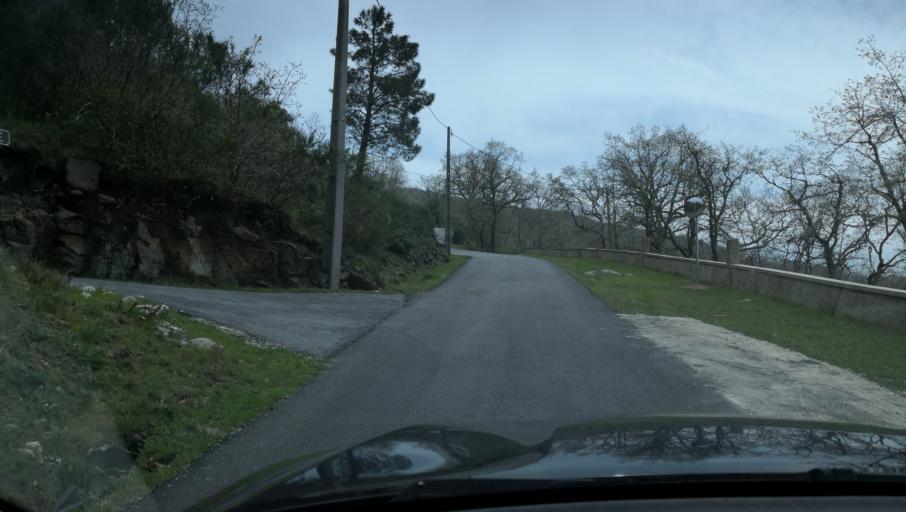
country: PT
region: Vila Real
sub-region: Vila Real
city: Vila Real
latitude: 41.2969
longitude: -7.8294
